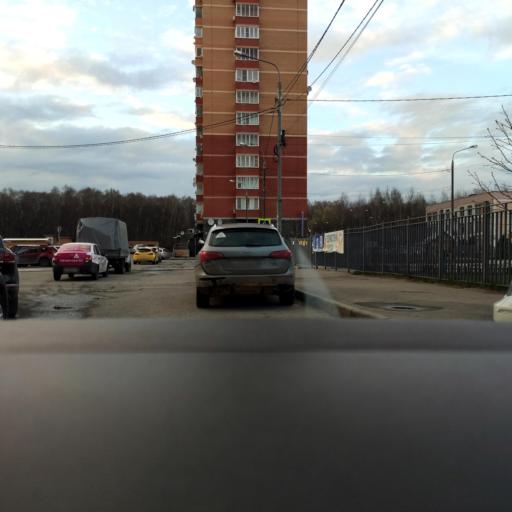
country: RU
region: Moskovskaya
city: Vidnoye
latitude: 55.5439
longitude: 37.7251
